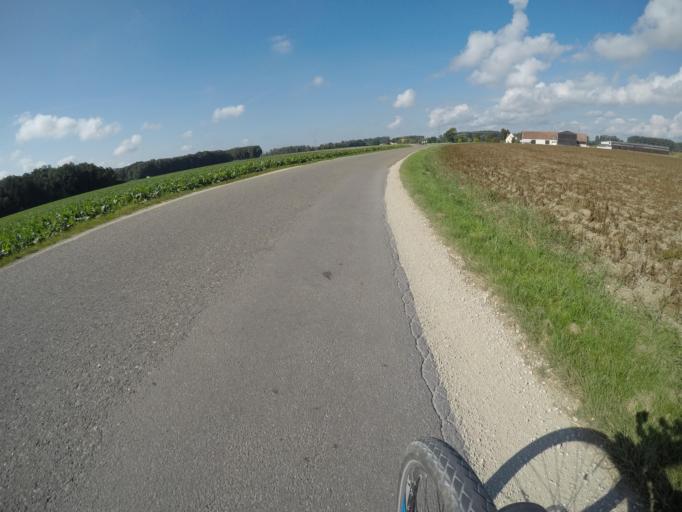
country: DE
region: Bavaria
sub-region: Swabia
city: Tapfheim
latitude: 48.6509
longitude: 10.7165
